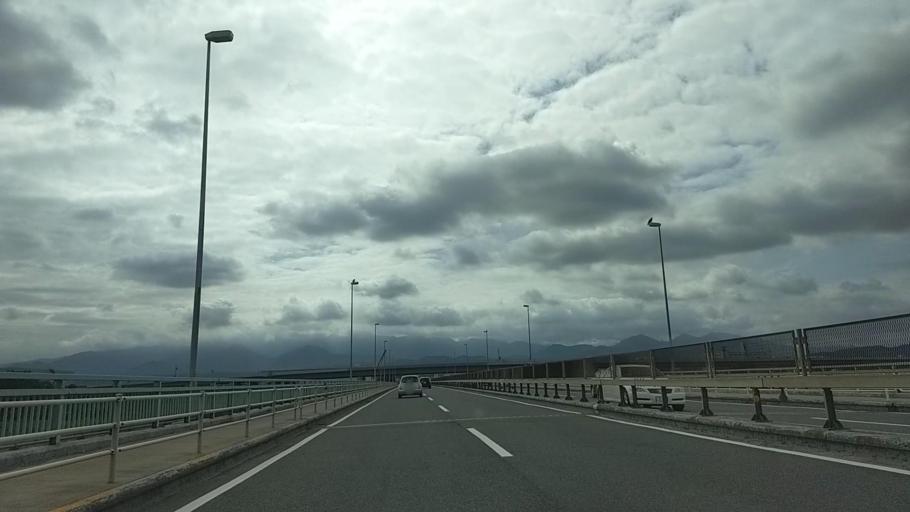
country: JP
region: Kanagawa
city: Zama
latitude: 35.4644
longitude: 139.3813
